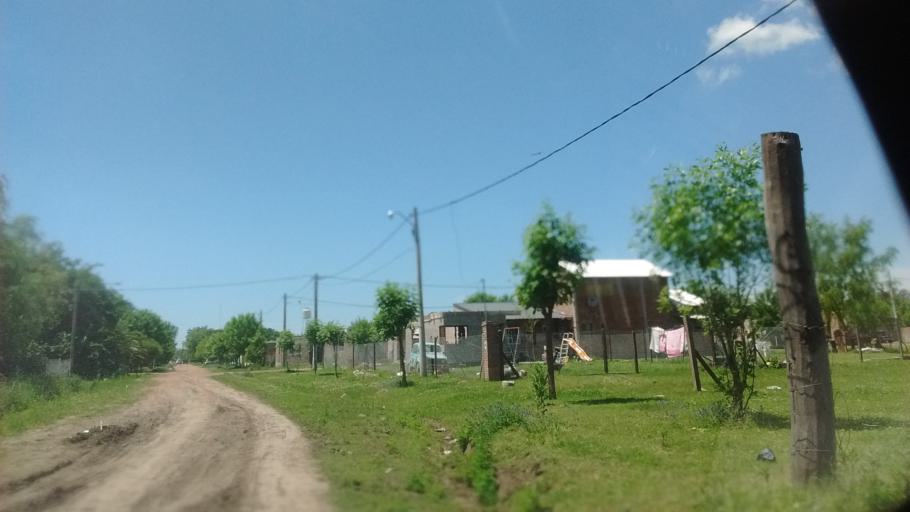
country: AR
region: Santa Fe
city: Funes
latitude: -32.8509
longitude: -60.7977
